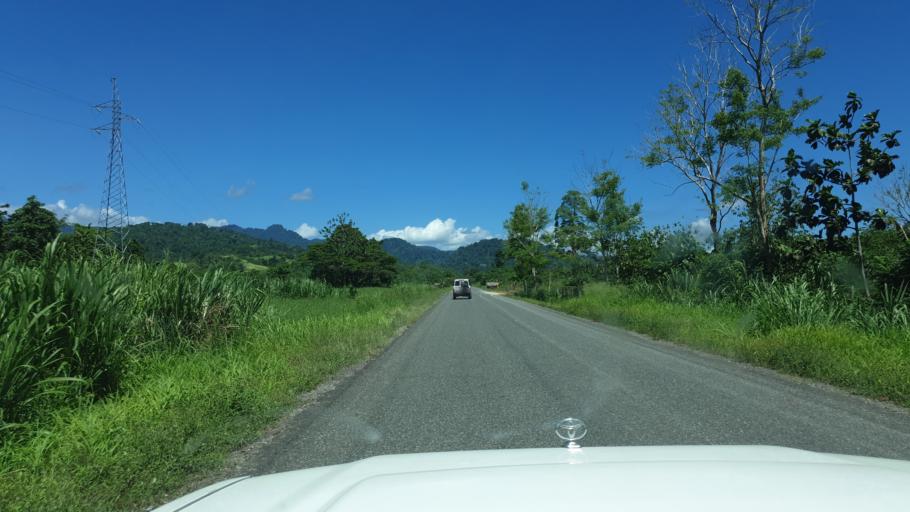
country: PG
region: Madang
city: Madang
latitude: -5.3973
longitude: 145.6639
